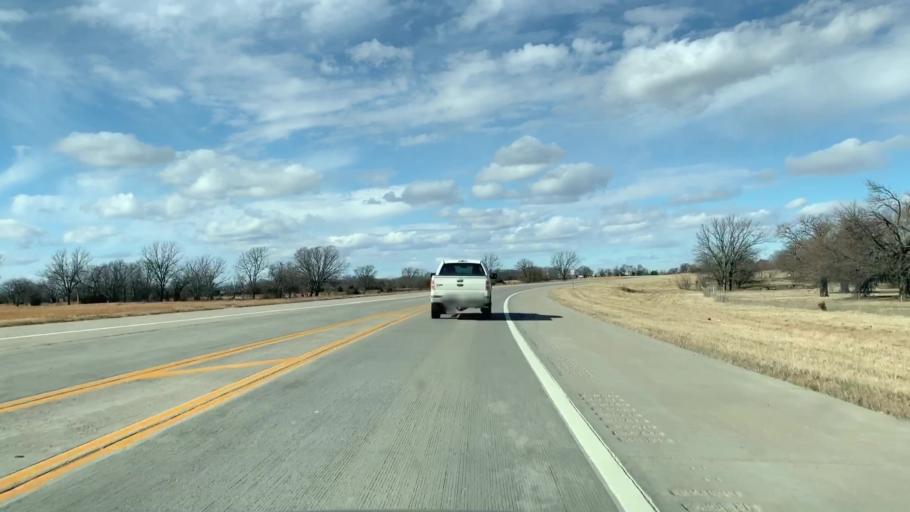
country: US
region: Kansas
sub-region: Labette County
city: Parsons
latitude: 37.3429
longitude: -95.1824
